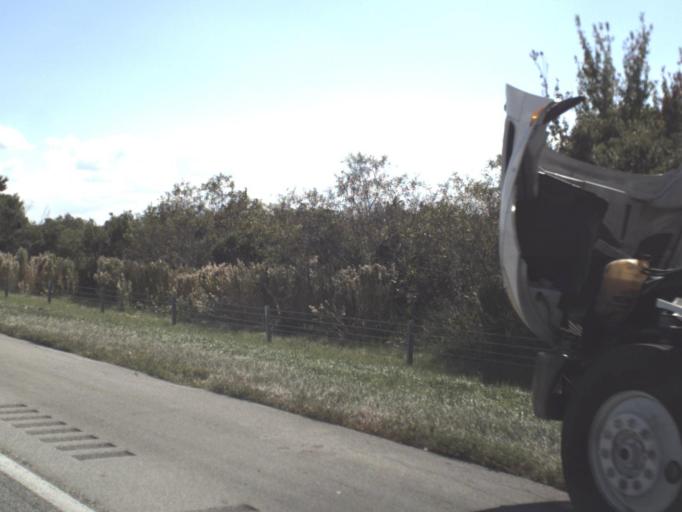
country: US
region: Florida
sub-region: Osceola County
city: Saint Cloud
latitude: 27.9276
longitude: -81.0639
